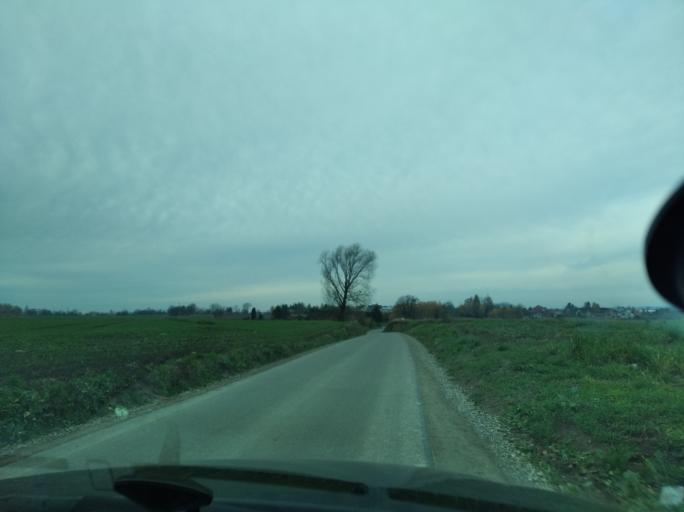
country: PL
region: Subcarpathian Voivodeship
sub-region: Powiat przeworski
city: Grzeska
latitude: 50.0696
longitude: 22.4601
